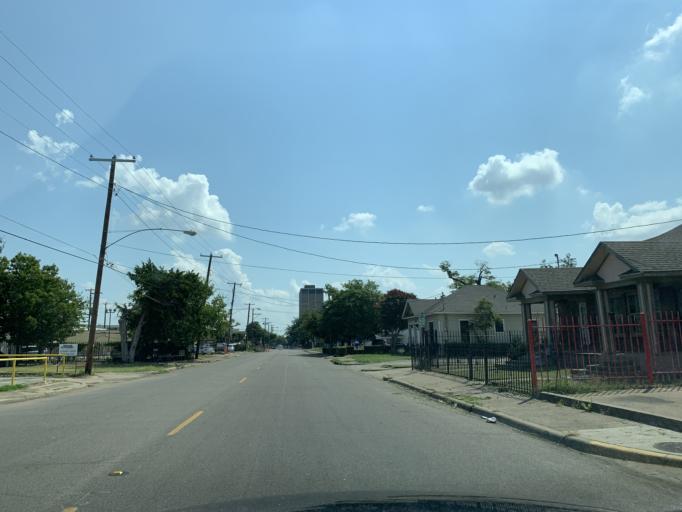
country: US
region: Texas
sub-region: Dallas County
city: Dallas
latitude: 32.7422
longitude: -96.8300
